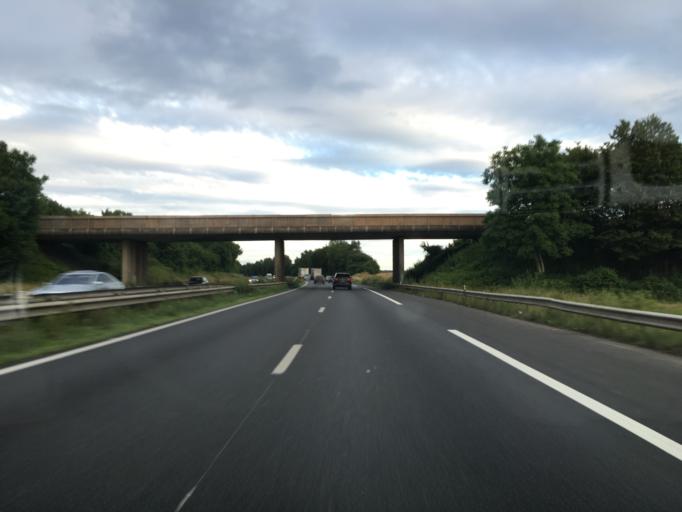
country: FR
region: Ile-de-France
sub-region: Departement de Seine-et-Marne
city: Brie-Comte-Robert
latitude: 48.6854
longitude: 2.5982
